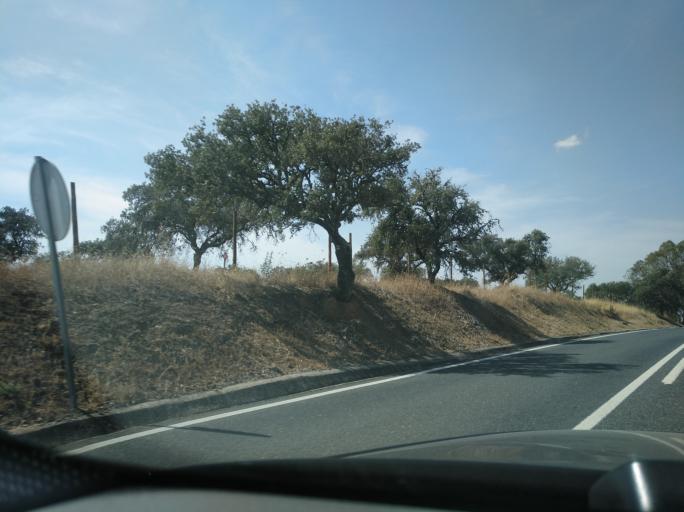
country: PT
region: Beja
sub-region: Mertola
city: Mertola
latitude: 37.7324
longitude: -7.7697
